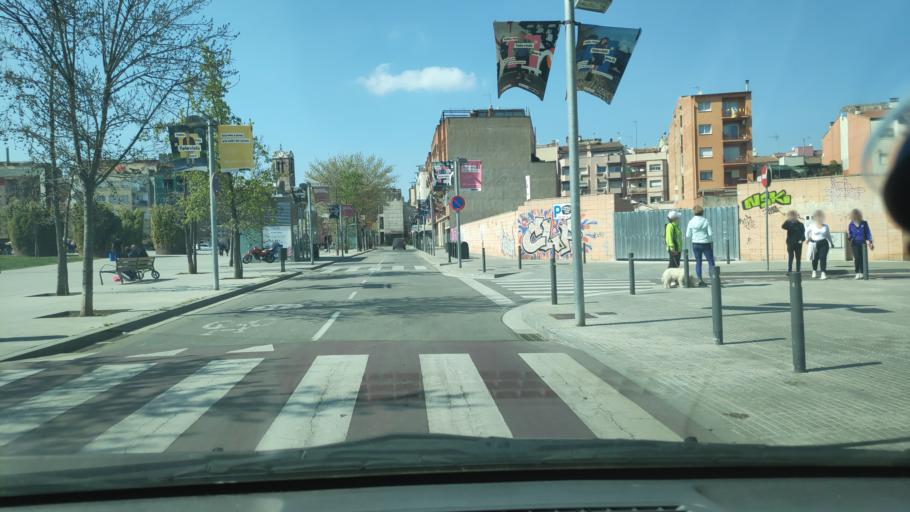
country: ES
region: Catalonia
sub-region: Provincia de Barcelona
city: Mollet del Valles
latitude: 41.5385
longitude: 2.2161
